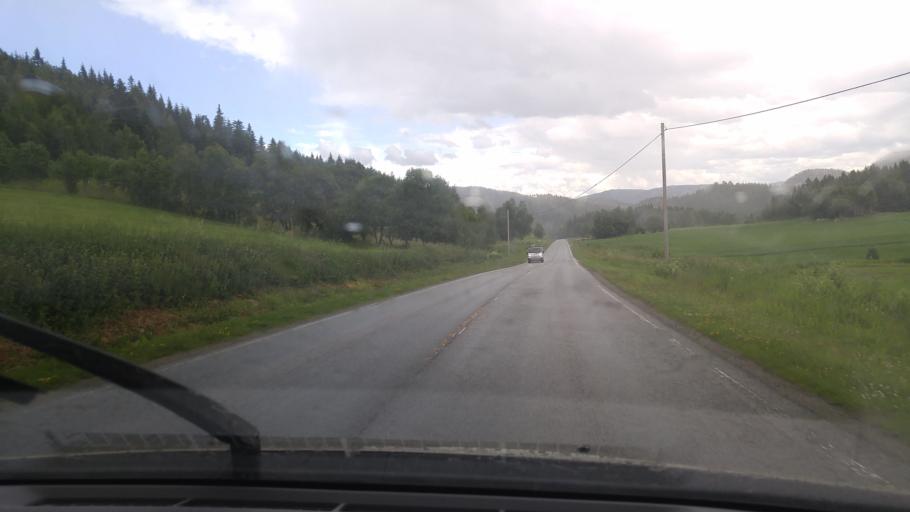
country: NO
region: Nord-Trondelag
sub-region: Namdalseid
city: Namdalseid
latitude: 64.3576
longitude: 11.2998
